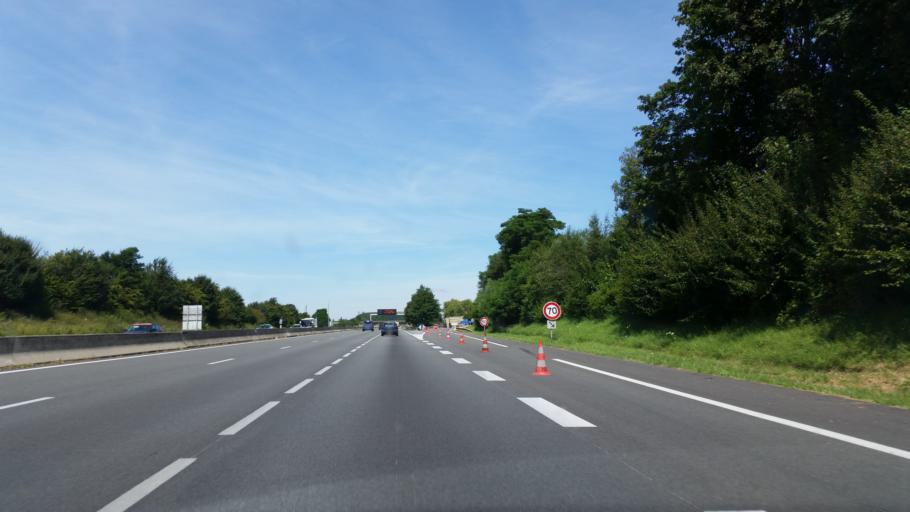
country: FR
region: Nord-Pas-de-Calais
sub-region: Departement du Pas-de-Calais
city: Bapaume
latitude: 50.0718
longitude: 2.8715
